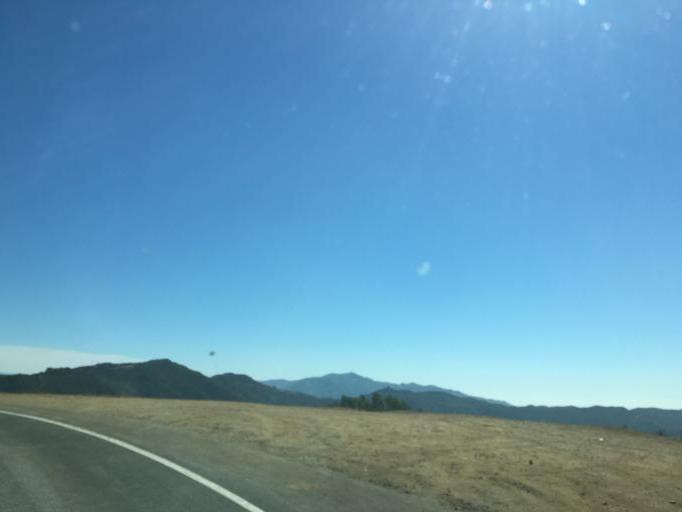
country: US
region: California
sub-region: Los Angeles County
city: Agoura Hills
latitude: 34.0727
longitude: -118.7536
